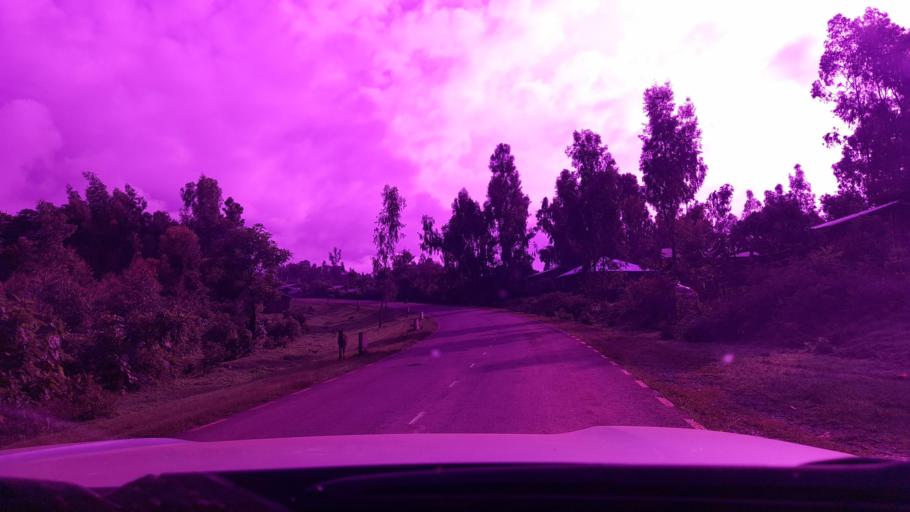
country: ET
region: Oromiya
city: Bedele
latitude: 8.2201
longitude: 36.4468
